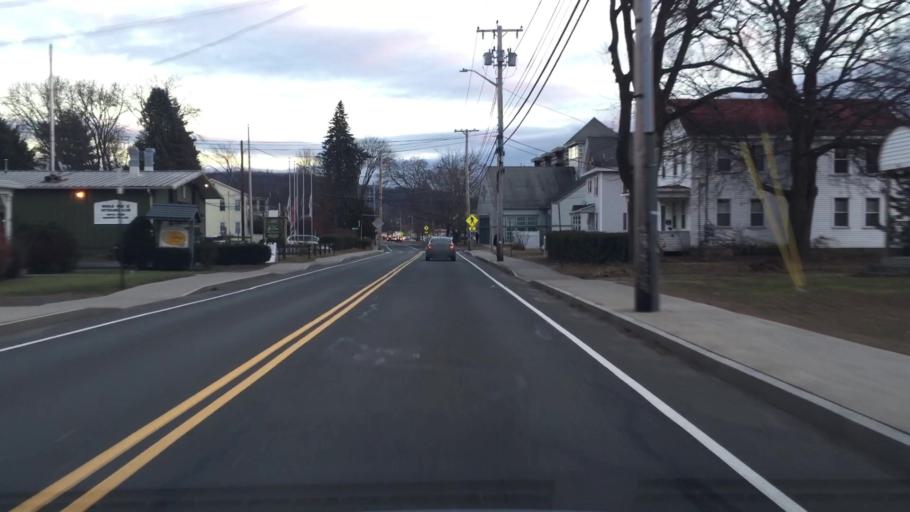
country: US
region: Massachusetts
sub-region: Hampshire County
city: Northampton
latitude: 42.3147
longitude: -72.6295
